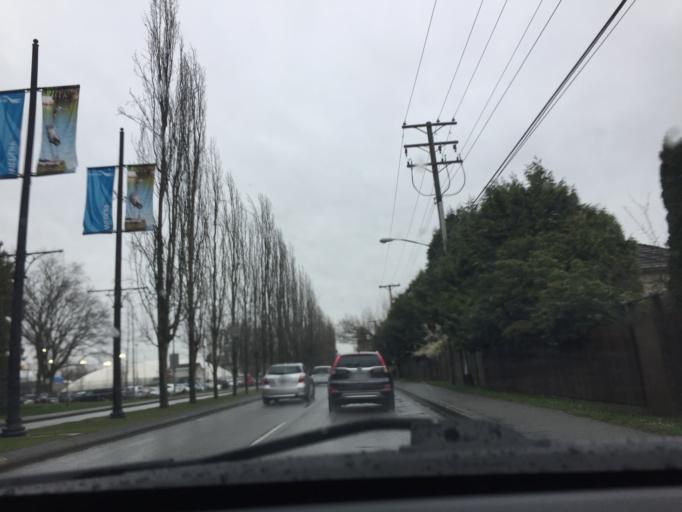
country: CA
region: British Columbia
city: Richmond
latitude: 49.1659
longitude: -123.1478
